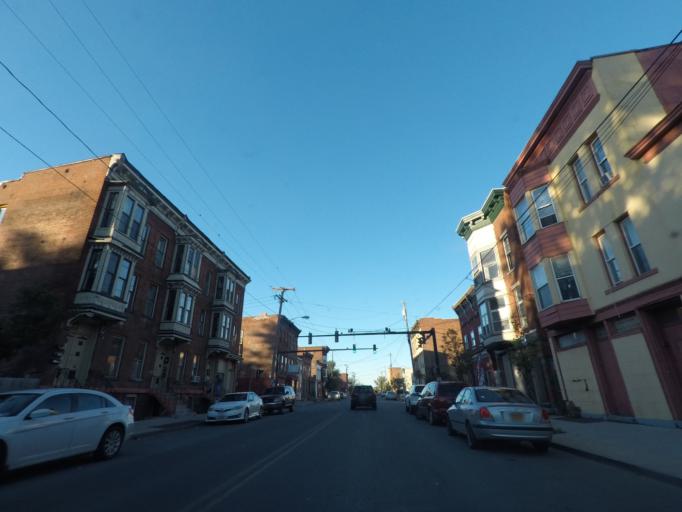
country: US
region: New York
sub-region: Albany County
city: Green Island
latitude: 42.7503
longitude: -73.6825
